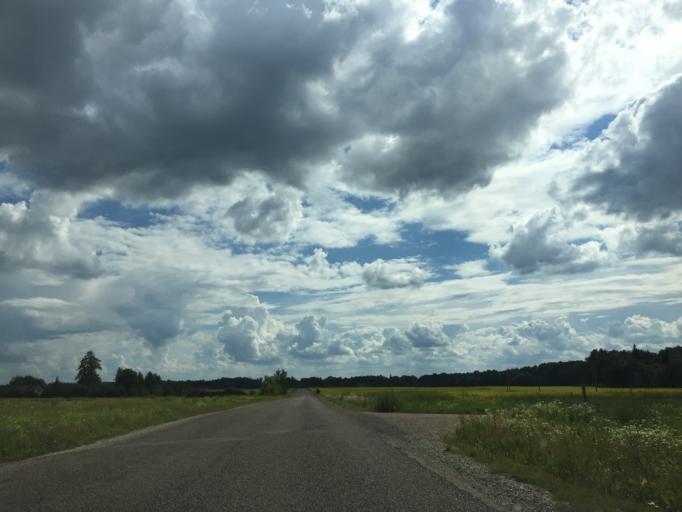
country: LV
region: Sigulda
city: Sigulda
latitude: 57.1924
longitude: 24.9430
